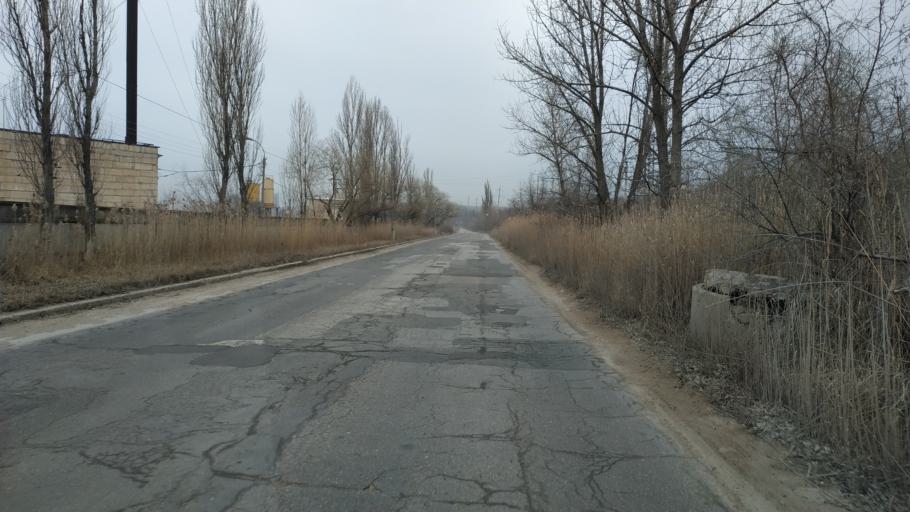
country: MD
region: Chisinau
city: Vatra
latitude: 47.0680
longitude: 28.7778
